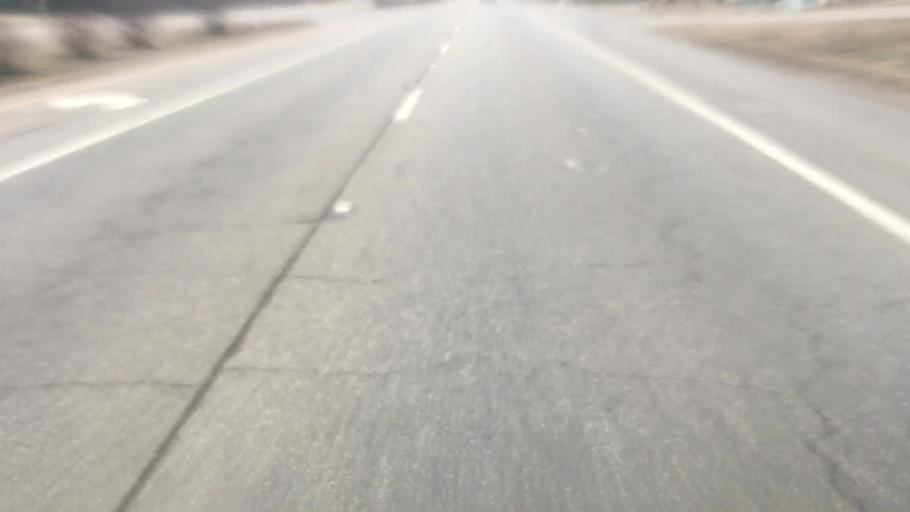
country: US
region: Alabama
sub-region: Walker County
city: Sumiton
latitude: 33.7408
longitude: -87.0362
